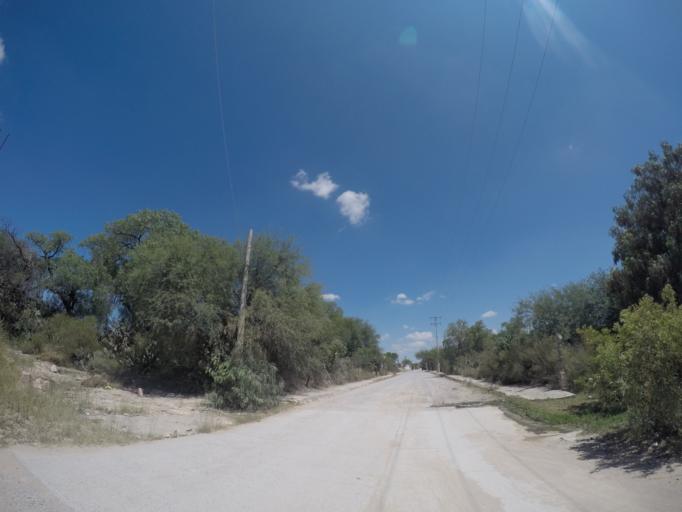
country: MX
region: San Luis Potosi
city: La Pila
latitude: 21.9981
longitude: -100.8983
